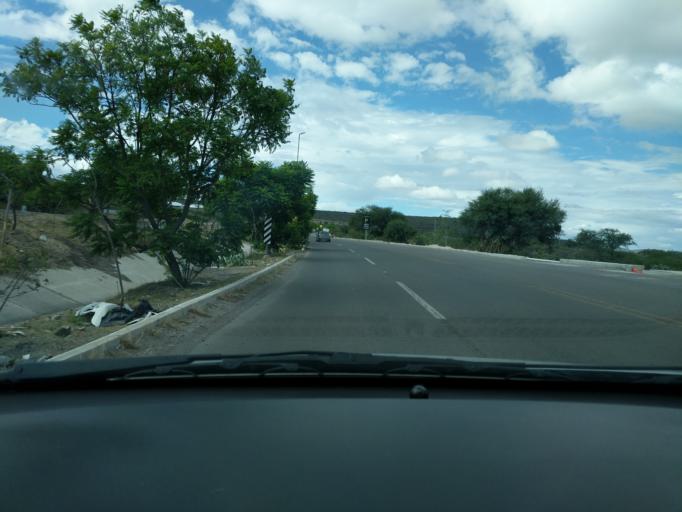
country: MX
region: Queretaro
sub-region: El Marques
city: La Pradera
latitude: 20.6666
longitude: -100.3124
